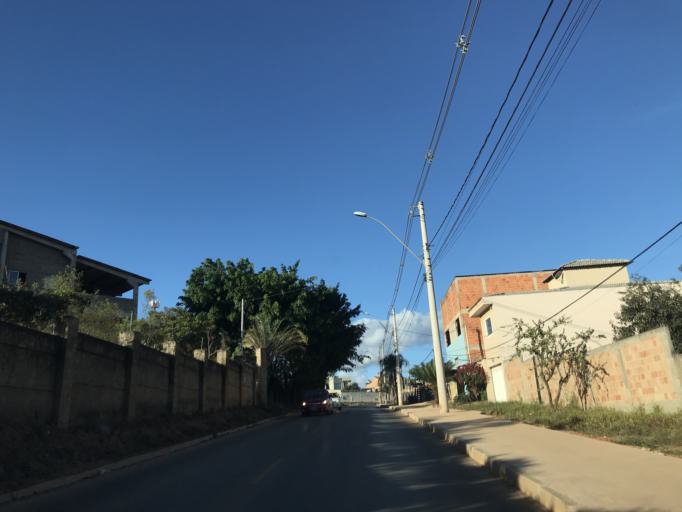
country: BR
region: Federal District
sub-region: Brasilia
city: Brasilia
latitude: -15.8832
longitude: -47.7689
